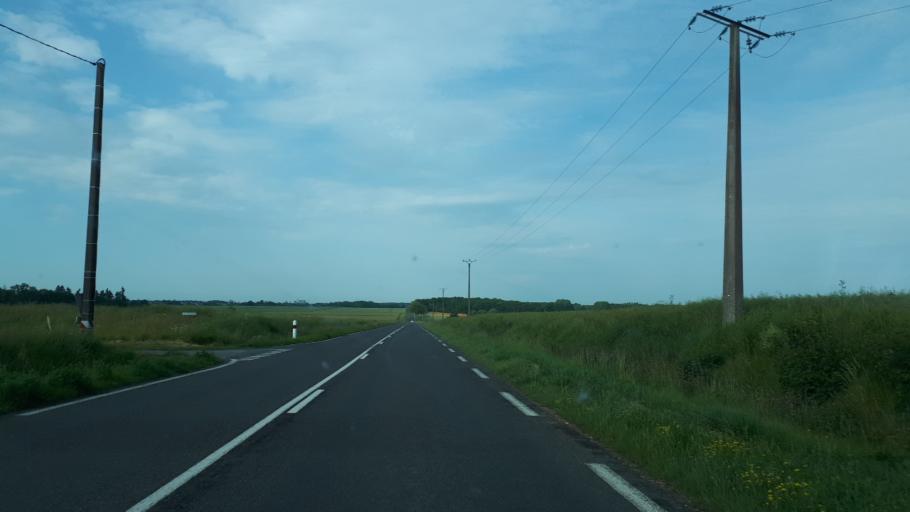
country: FR
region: Centre
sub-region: Departement d'Indre-et-Loire
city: Monnaie
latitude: 47.5212
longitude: 0.8215
